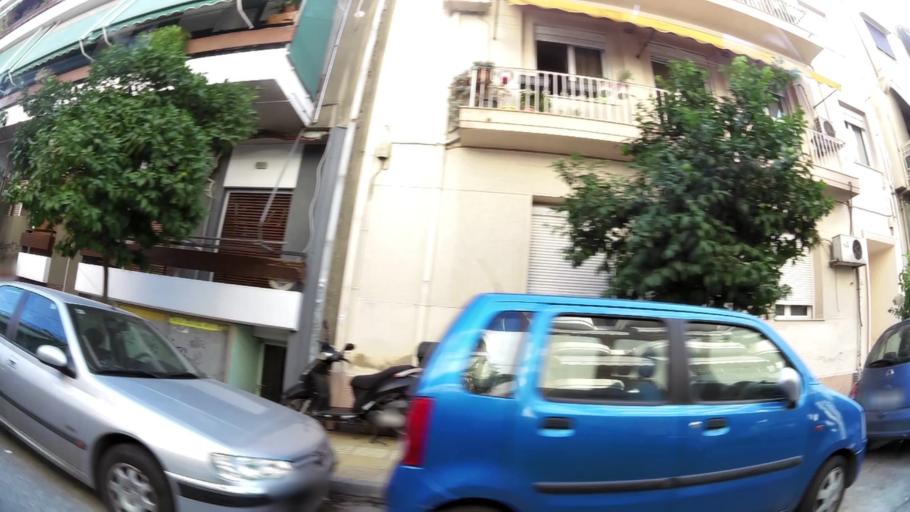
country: GR
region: Attica
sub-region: Nomarchia Athinas
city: Athens
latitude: 37.9701
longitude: 23.7088
